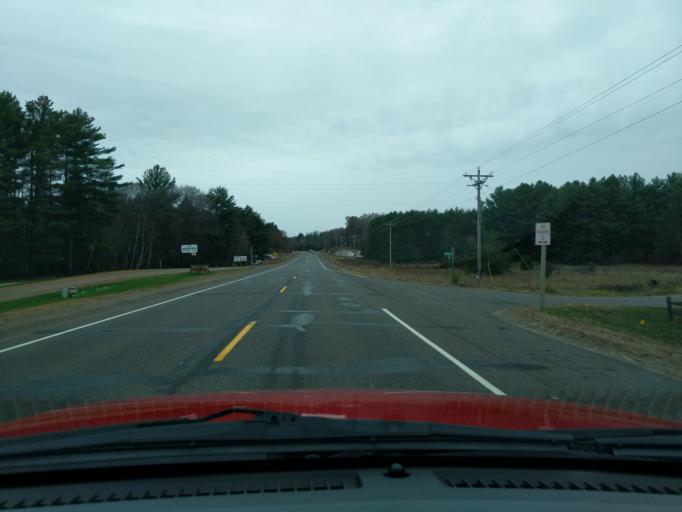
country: US
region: Wisconsin
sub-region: Burnett County
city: Siren
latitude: 45.8191
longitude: -92.3289
